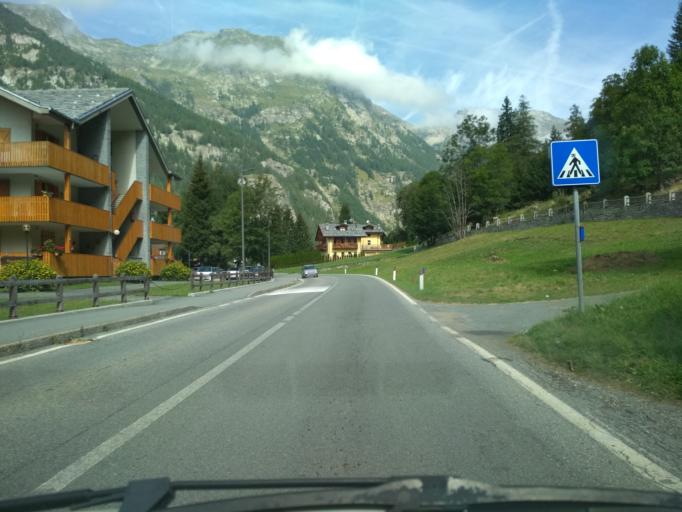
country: IT
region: Aosta Valley
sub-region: Valle d'Aosta
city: Gressoney-Saint-Jean
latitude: 45.7699
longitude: 7.8325
